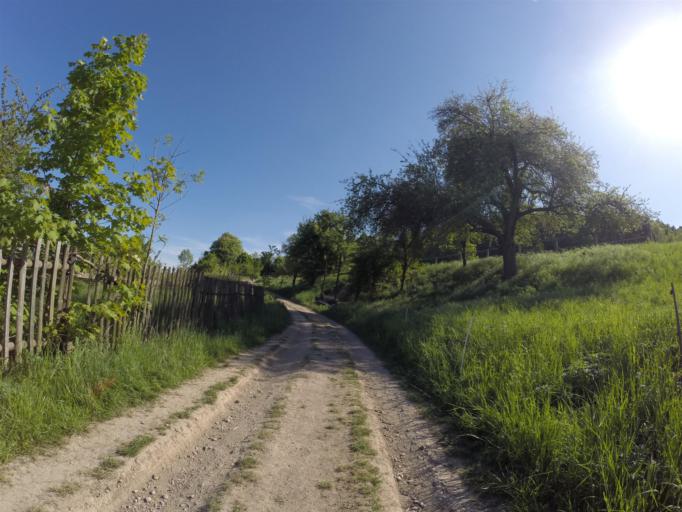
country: DE
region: Thuringia
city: Neuengonna
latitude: 50.9853
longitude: 11.6529
